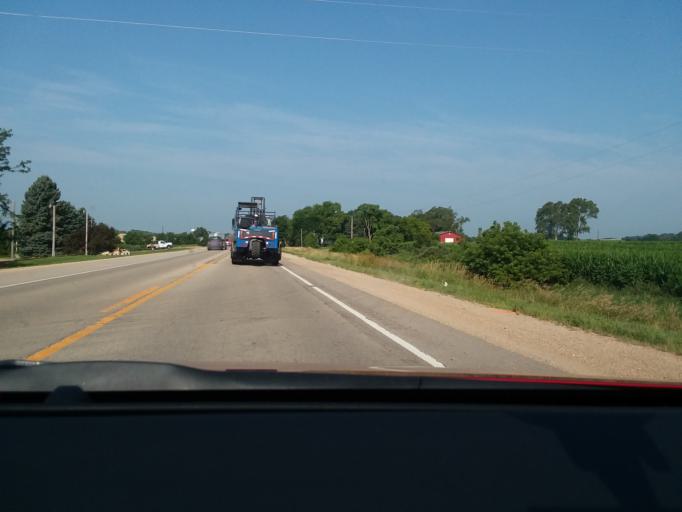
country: US
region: Wisconsin
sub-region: Dane County
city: Waunakee
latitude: 43.1921
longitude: -89.4016
